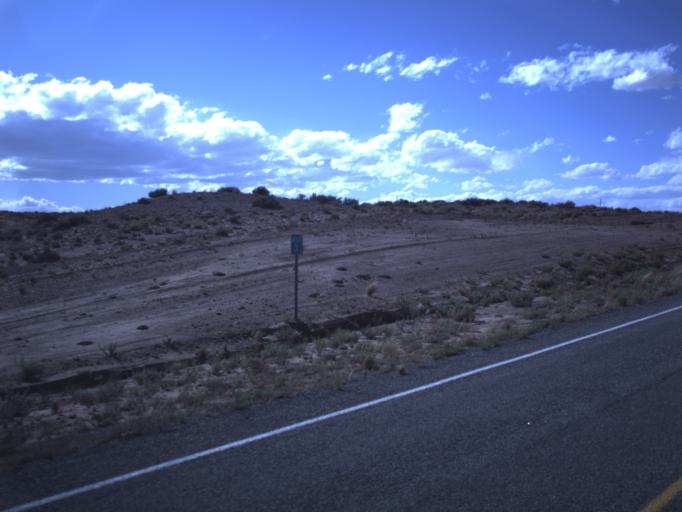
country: US
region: Utah
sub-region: Emery County
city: Ferron
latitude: 38.3345
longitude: -110.6839
